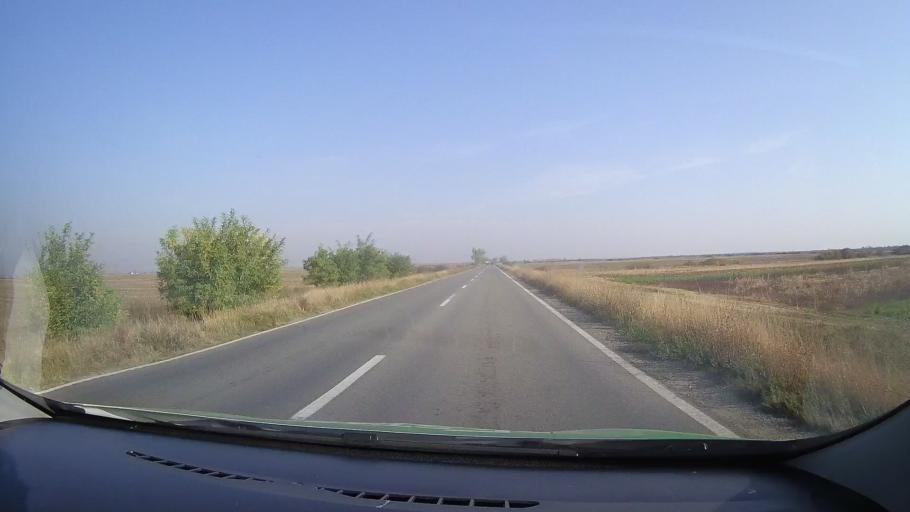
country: RO
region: Arad
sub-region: Comuna Pilu
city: Pilu
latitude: 46.5887
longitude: 21.3457
